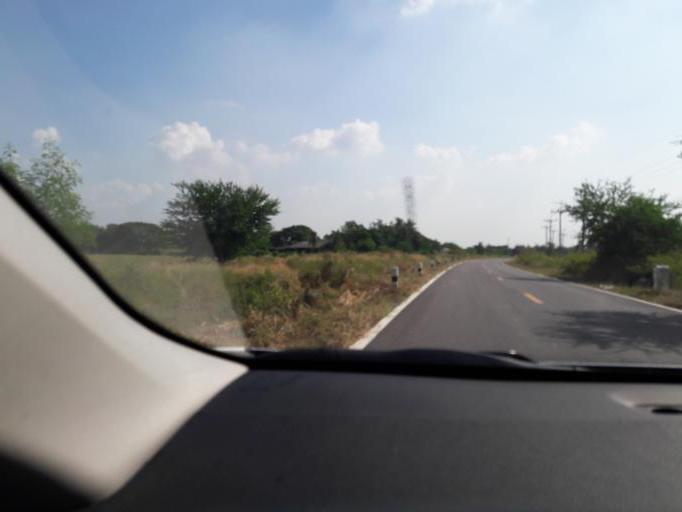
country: TH
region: Ang Thong
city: Wiset Chaichan
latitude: 14.5609
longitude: 100.3896
